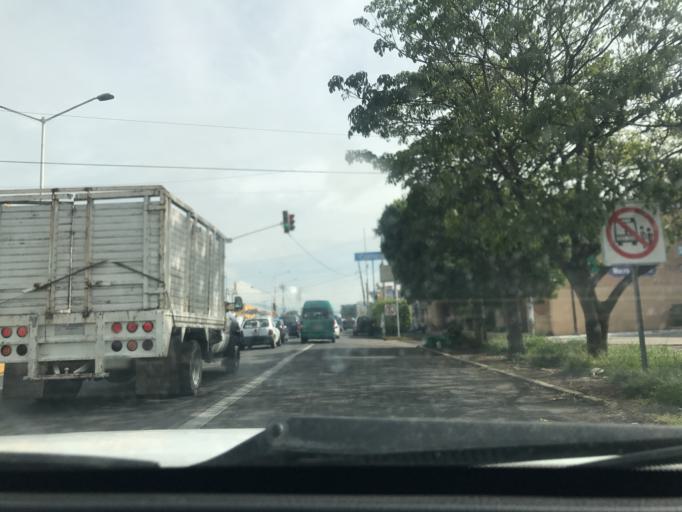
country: MX
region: Morelos
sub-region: Cuautla
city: Tierra Larga (Campo Nuevo)
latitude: 18.8654
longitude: -98.9300
